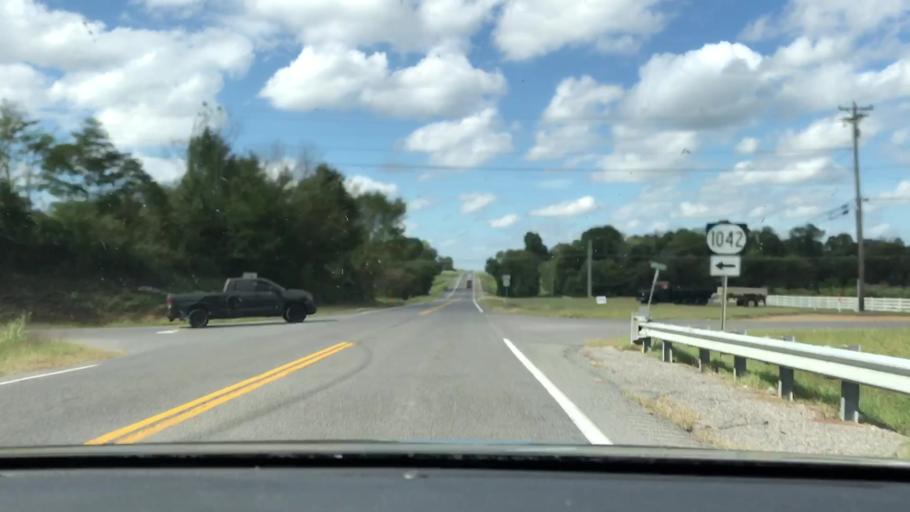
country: US
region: Kentucky
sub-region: Livingston County
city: Ledbetter
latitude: 37.0070
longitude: -88.4682
